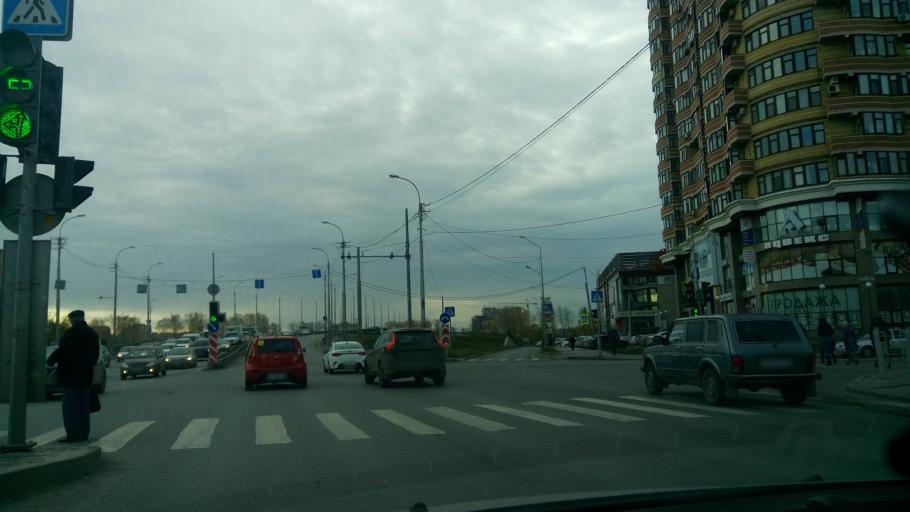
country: RU
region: Tjumen
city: Tyumen
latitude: 57.1348
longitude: 65.5653
